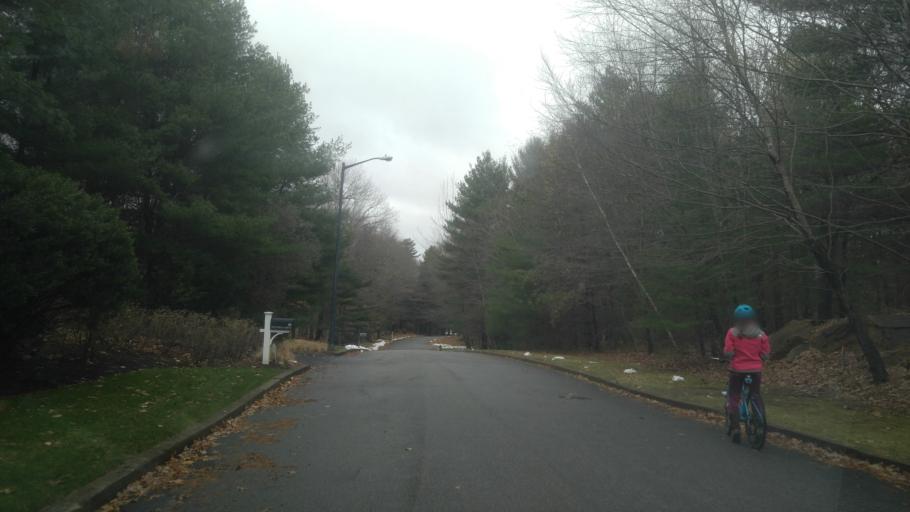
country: US
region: Rhode Island
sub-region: Kent County
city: West Warwick
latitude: 41.6476
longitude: -71.5341
